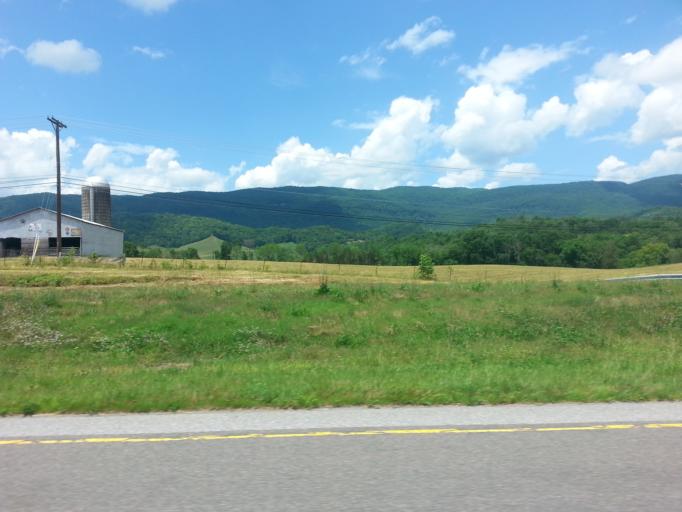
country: US
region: Tennessee
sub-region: Claiborne County
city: Harrogate
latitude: 36.6053
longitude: -83.5882
